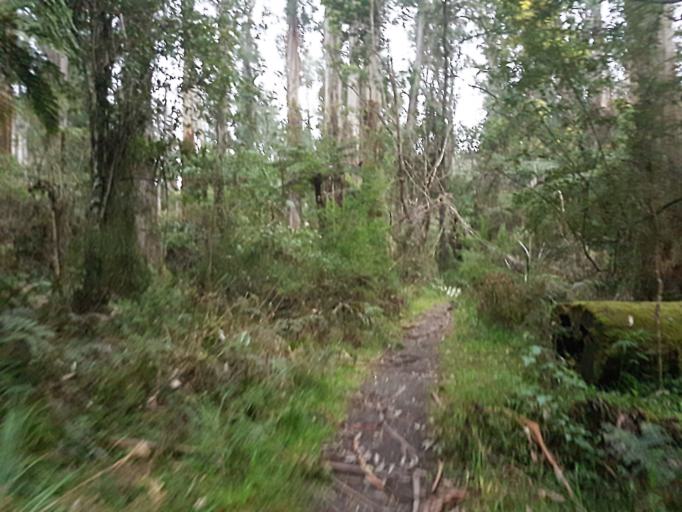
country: AU
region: Victoria
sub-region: Yarra Ranges
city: Belgrave
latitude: -37.8970
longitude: 145.3568
